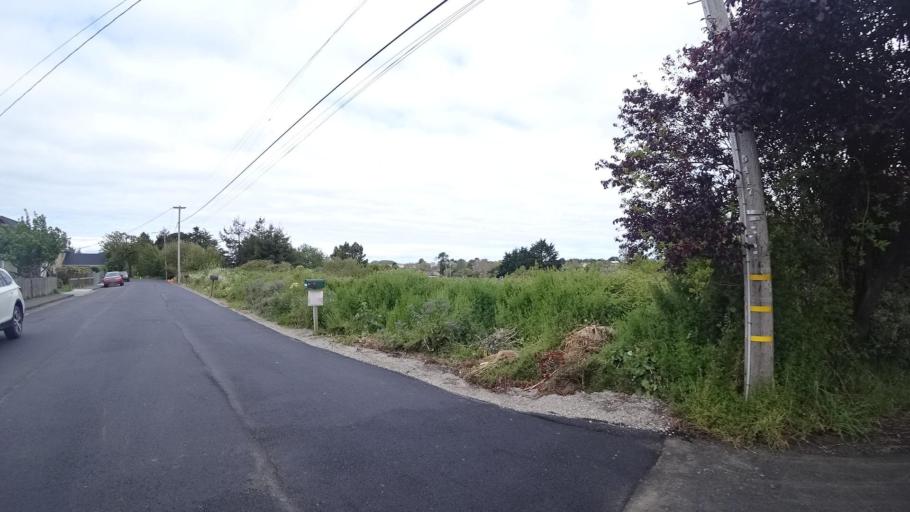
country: US
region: California
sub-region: Humboldt County
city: Arcata
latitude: 40.8818
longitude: -124.0903
